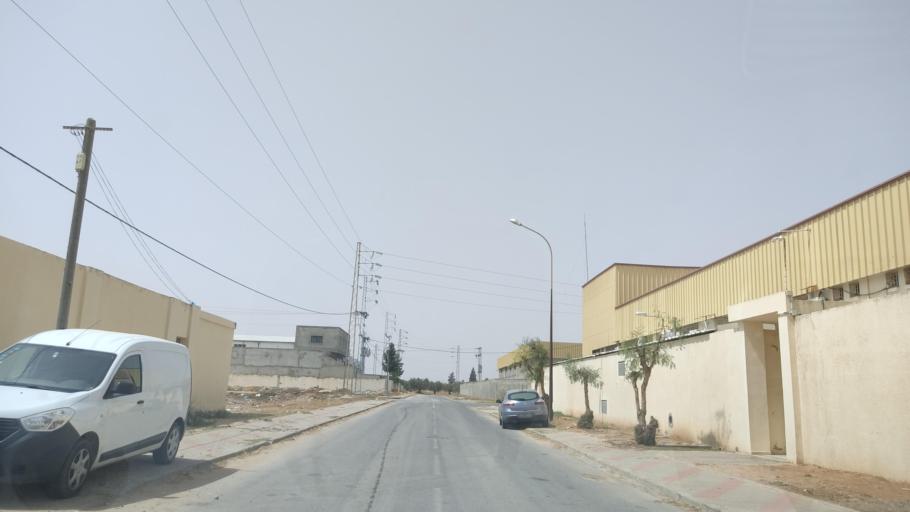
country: TN
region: Al Mahdiyah
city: El Jem
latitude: 35.1290
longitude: 10.7377
